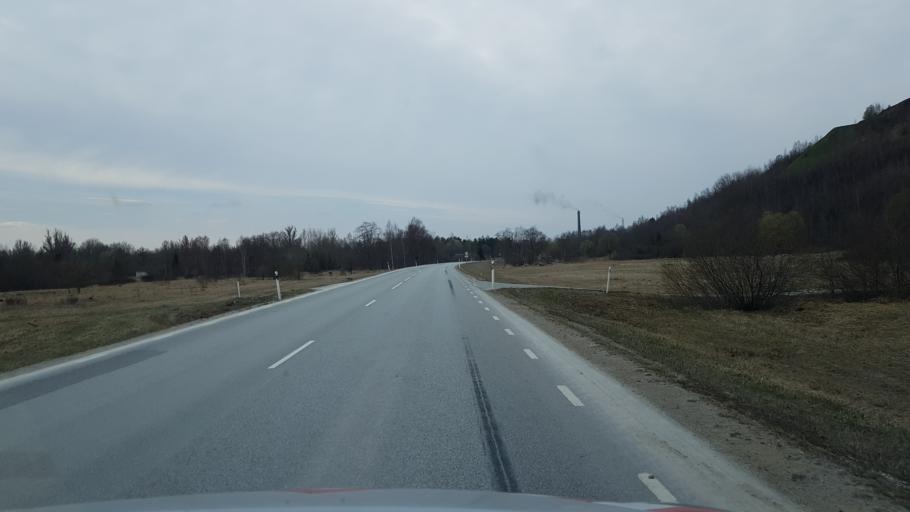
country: EE
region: Ida-Virumaa
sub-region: Kivioli linn
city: Kivioli
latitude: 59.3627
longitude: 26.9615
